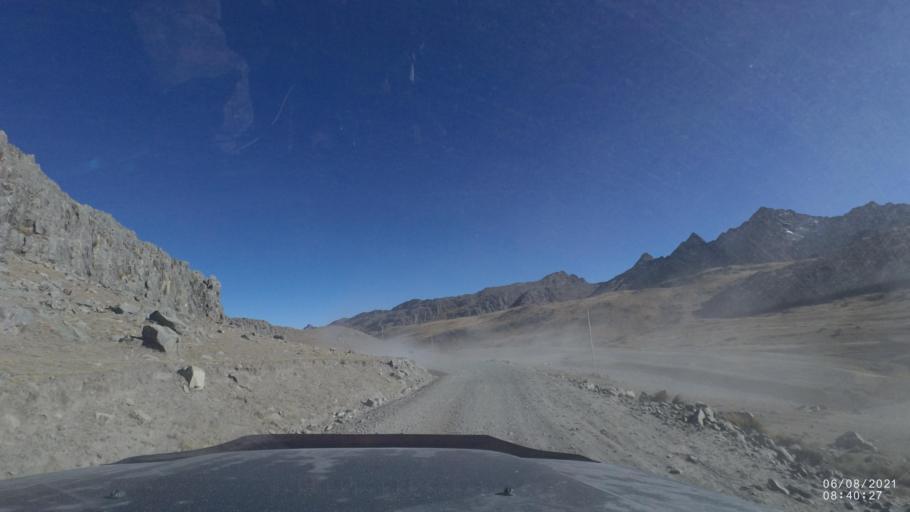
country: BO
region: Cochabamba
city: Sipe Sipe
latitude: -17.1728
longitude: -66.4003
